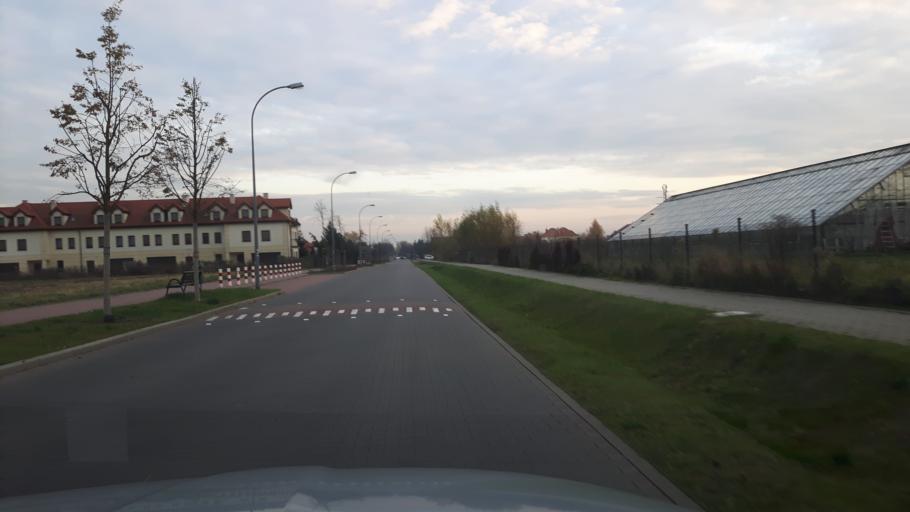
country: PL
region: Masovian Voivodeship
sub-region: Warszawa
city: Wilanow
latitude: 52.1780
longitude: 21.1082
